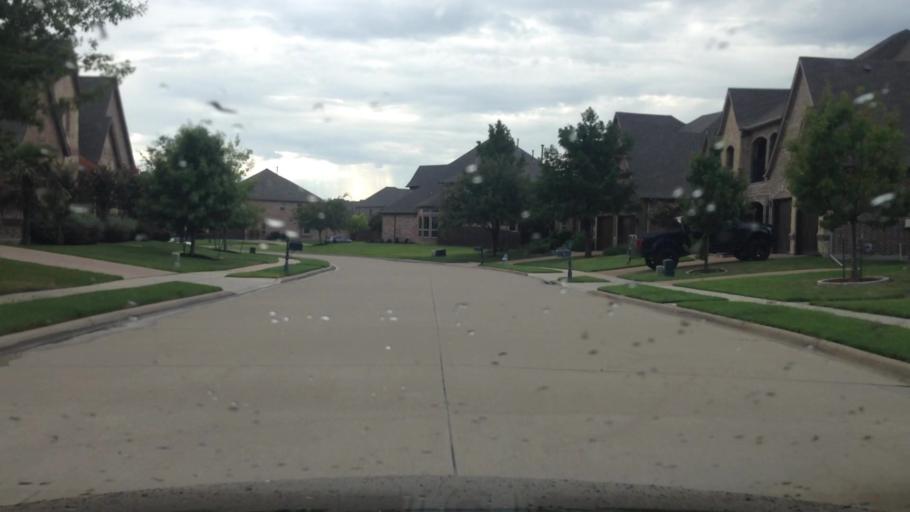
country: US
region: Texas
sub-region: Denton County
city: Lewisville
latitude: 33.0059
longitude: -97.0284
